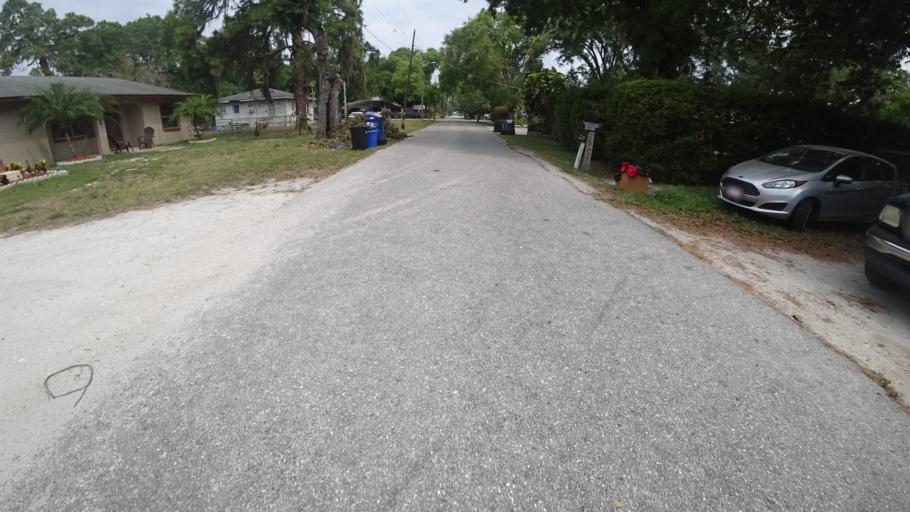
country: US
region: Florida
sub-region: Manatee County
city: Samoset
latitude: 27.4671
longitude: -82.5395
